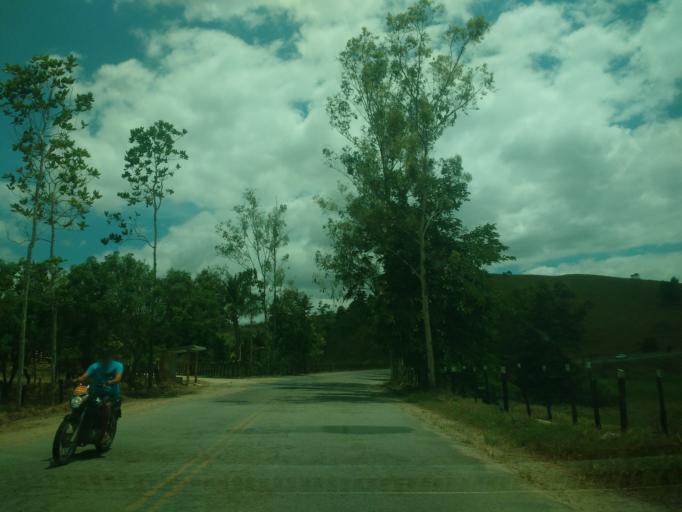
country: BR
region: Alagoas
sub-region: Santana Do Mundau
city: Santana do Mundau
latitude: -9.1492
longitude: -36.1706
